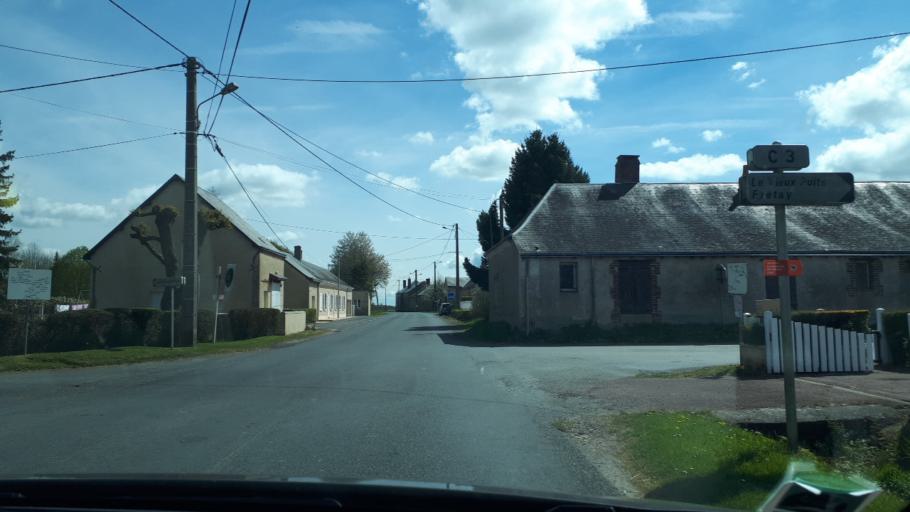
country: FR
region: Centre
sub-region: Departement du Loir-et-Cher
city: Savigny-sur-Braye
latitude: 47.8644
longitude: 0.8595
